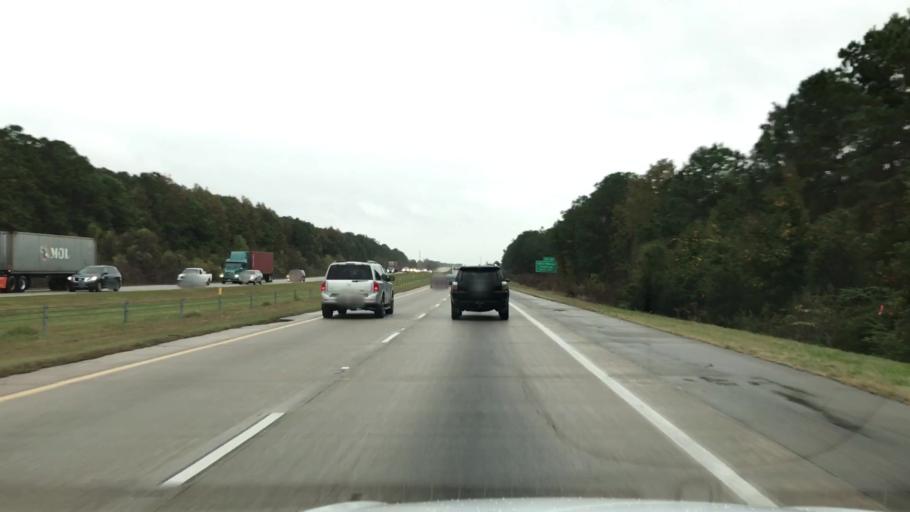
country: US
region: South Carolina
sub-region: Charleston County
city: Mount Pleasant
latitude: 32.8446
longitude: -79.8725
